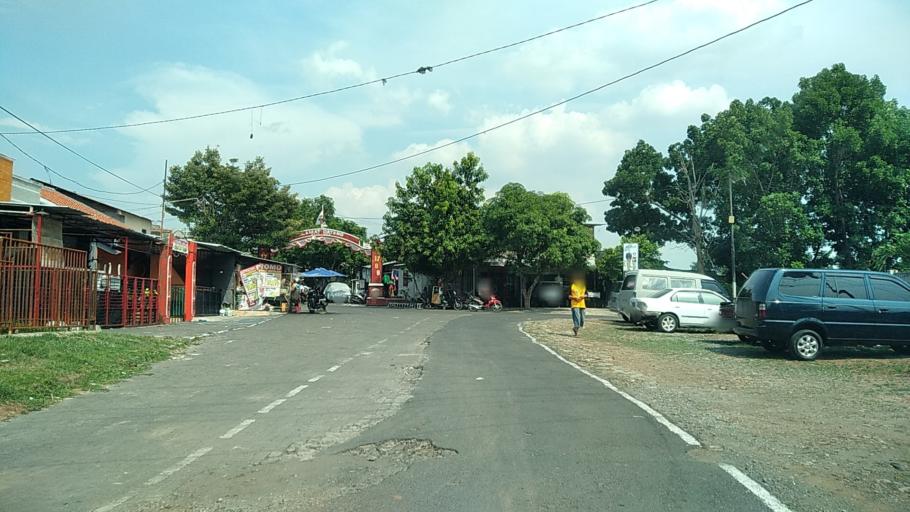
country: ID
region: Central Java
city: Semarang
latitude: -6.9941
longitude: 110.3910
